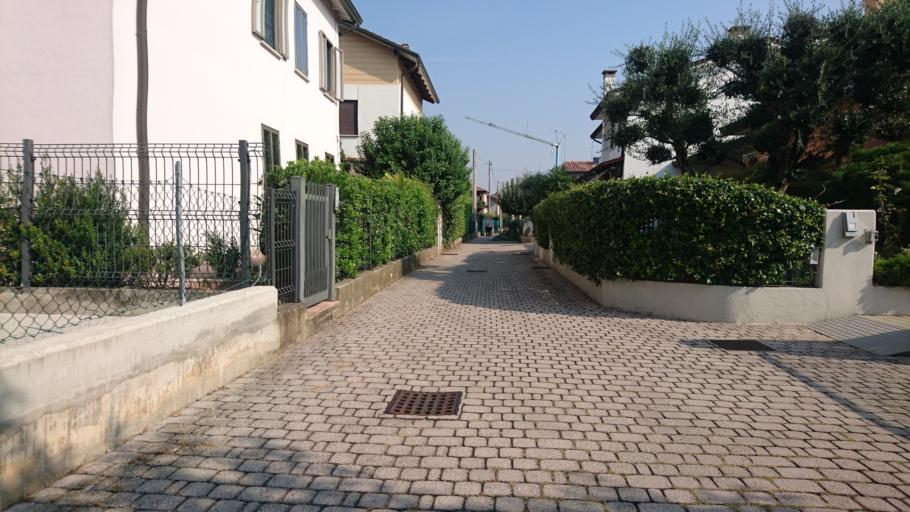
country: IT
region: Veneto
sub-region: Provincia di Padova
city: Albignasego
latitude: 45.3471
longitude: 11.8653
